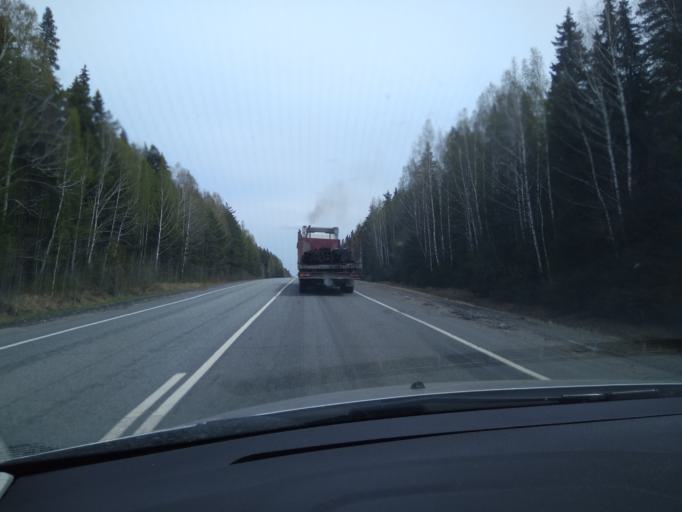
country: RU
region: Sverdlovsk
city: Yushala
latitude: 57.1067
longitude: 64.2070
